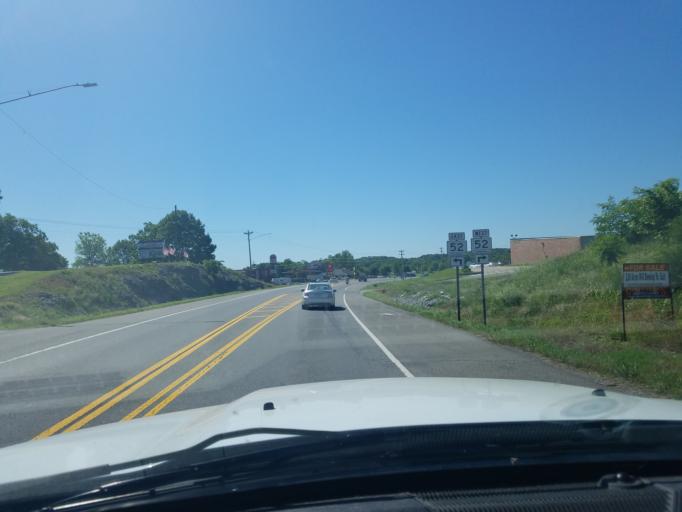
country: US
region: Tennessee
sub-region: Sumner County
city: Westmoreland
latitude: 36.5551
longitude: -86.2383
